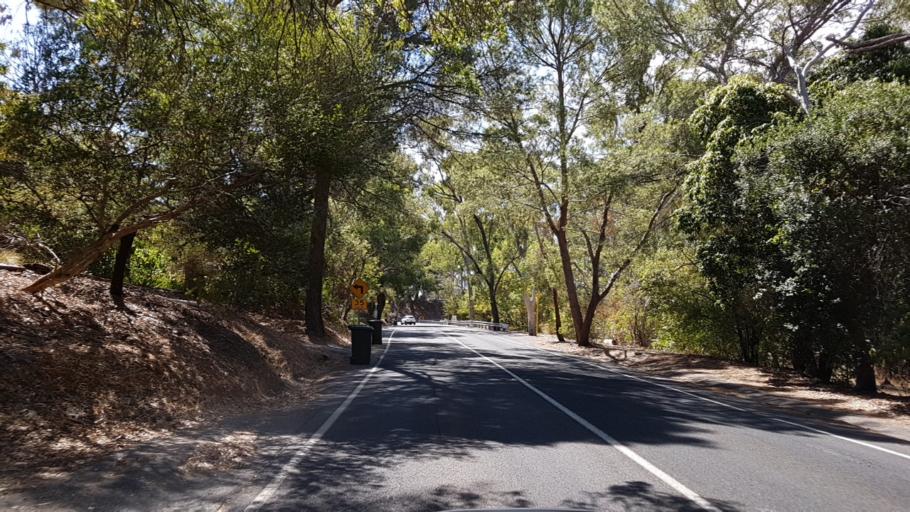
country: AU
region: South Australia
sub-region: Mitcham
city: Belair
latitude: -35.0000
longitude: 138.6326
